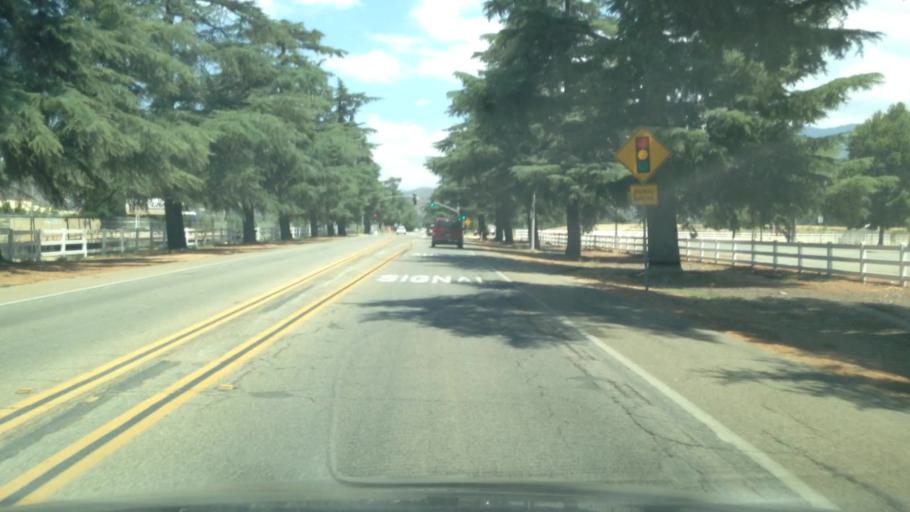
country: US
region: California
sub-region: Riverside County
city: Cherry Valley
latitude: 33.9598
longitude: -116.9773
